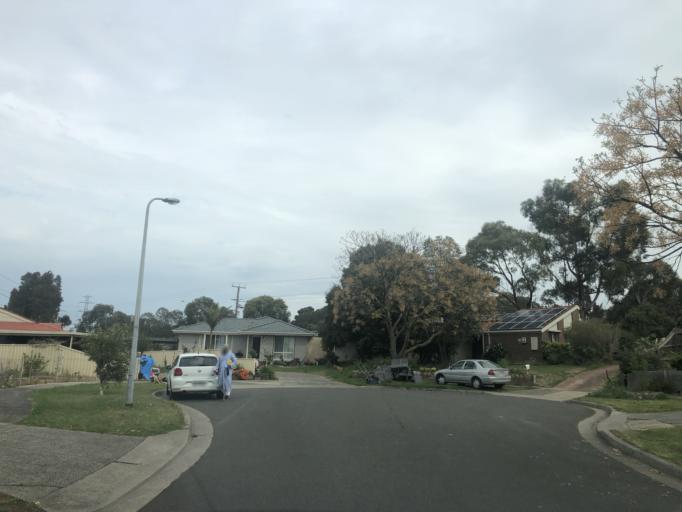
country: AU
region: Victoria
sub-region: Casey
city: Hallam
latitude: -38.0097
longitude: 145.2827
